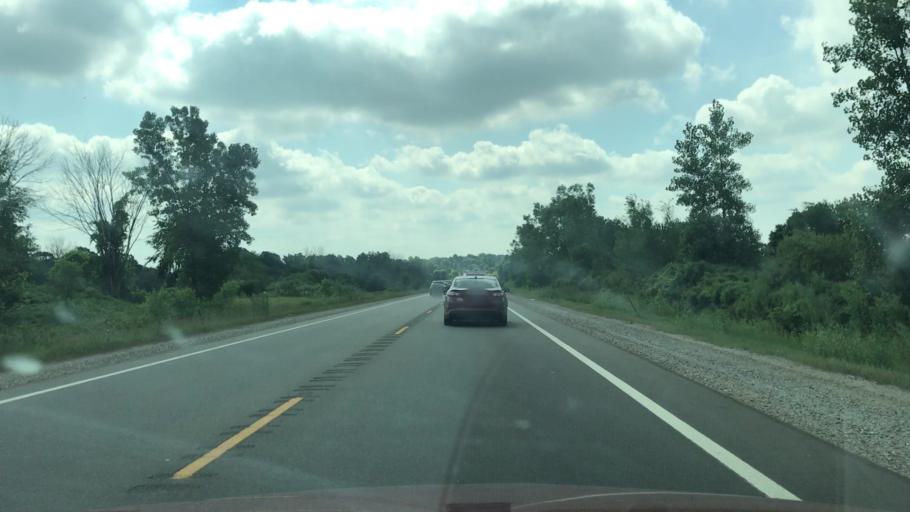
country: US
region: Michigan
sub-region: Kent County
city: Kent City
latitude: 43.2043
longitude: -85.7363
